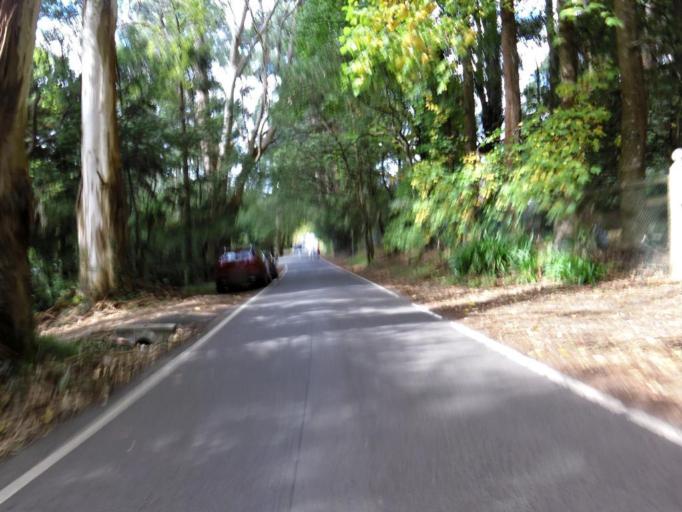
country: AU
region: Victoria
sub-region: Yarra Ranges
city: Olinda
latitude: -37.8565
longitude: 145.3618
